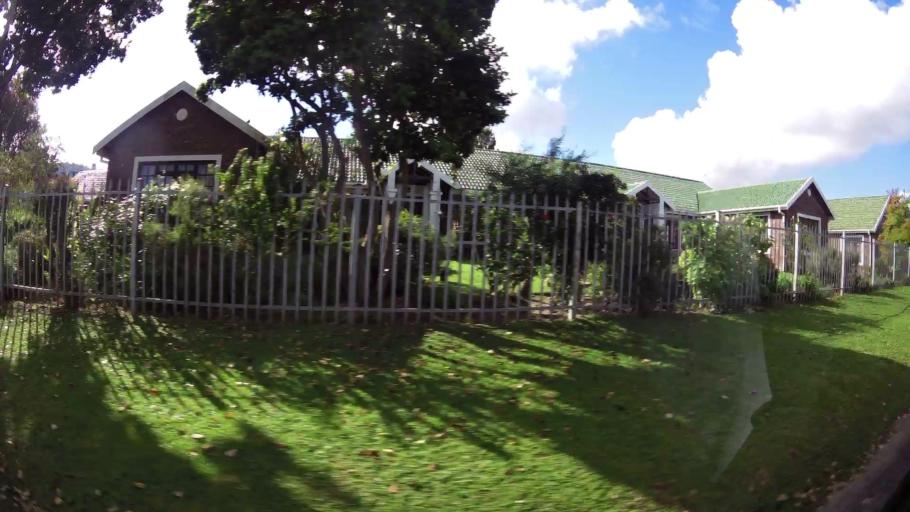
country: ZA
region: Western Cape
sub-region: Eden District Municipality
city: Knysna
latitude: -34.0418
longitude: 23.0687
